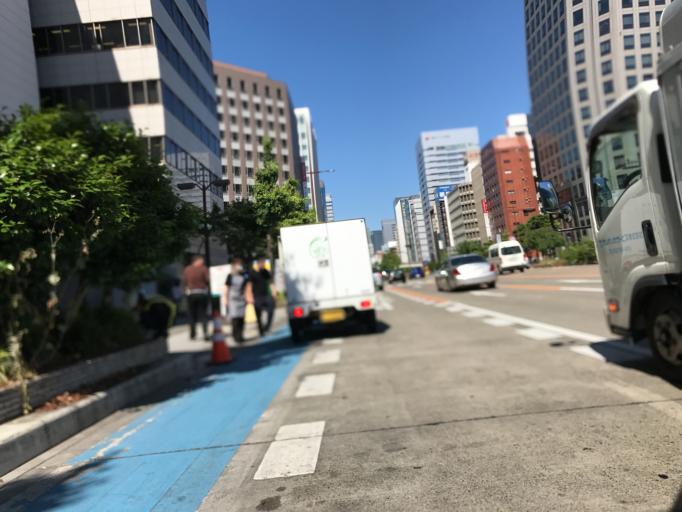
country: JP
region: Aichi
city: Nagoya-shi
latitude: 35.1736
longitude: 136.9073
